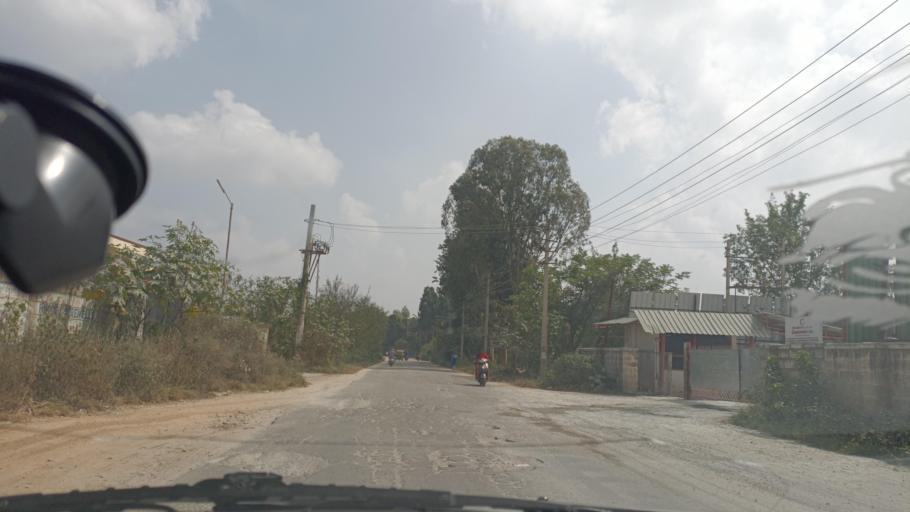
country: IN
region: Karnataka
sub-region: Bangalore Urban
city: Yelahanka
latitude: 13.1603
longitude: 77.6327
